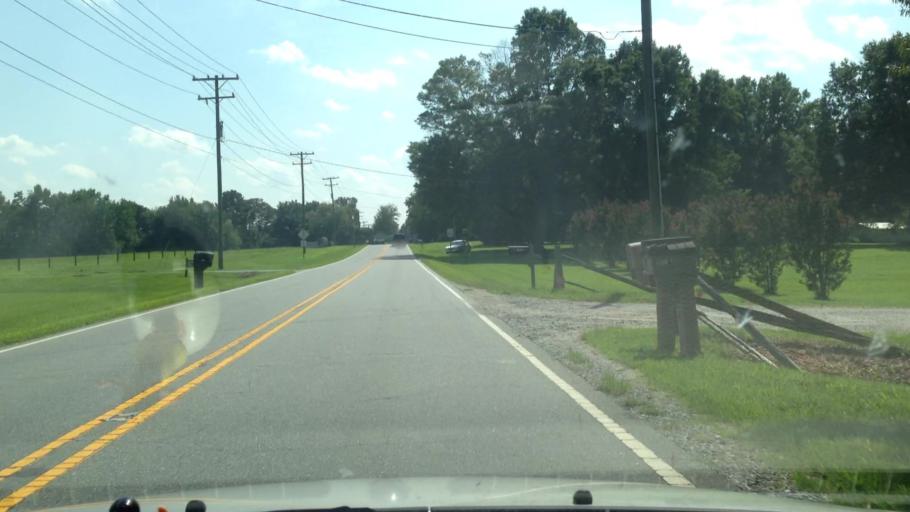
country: US
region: North Carolina
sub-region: Forsyth County
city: Kernersville
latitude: 36.1525
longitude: -80.0356
